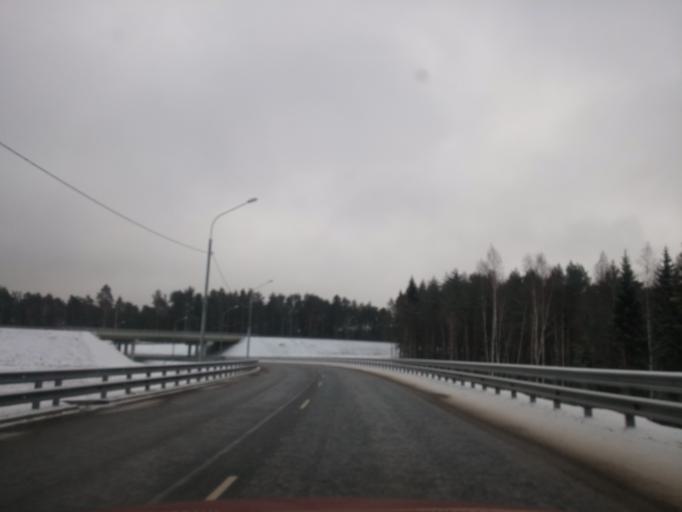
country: RU
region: Tverskaya
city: Likhoslavl'
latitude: 56.9459
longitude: 35.4947
